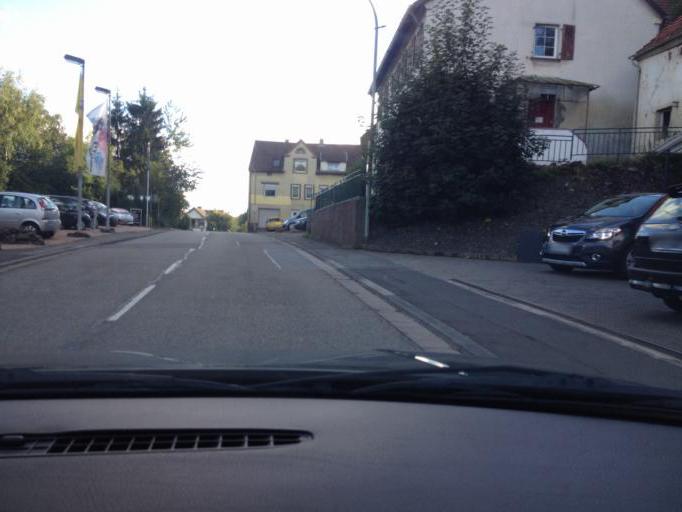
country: DE
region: Saarland
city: Marpingen
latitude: 49.4307
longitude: 7.0251
